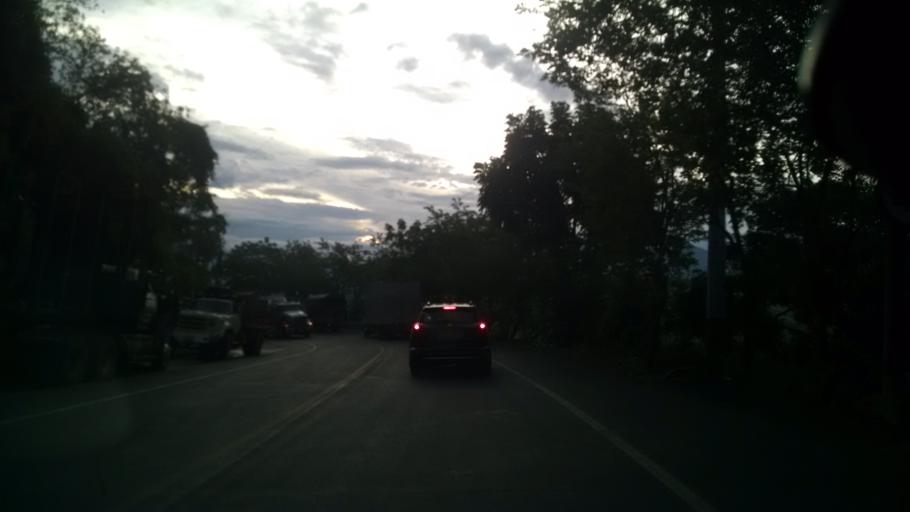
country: CO
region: Antioquia
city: Santa Barbara
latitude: 5.8414
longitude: -75.5804
